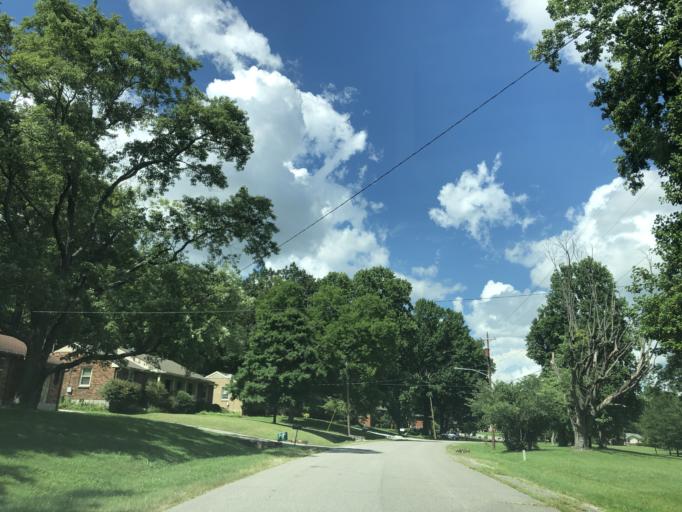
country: US
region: Tennessee
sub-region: Davidson County
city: Oak Hill
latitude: 36.0754
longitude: -86.7330
